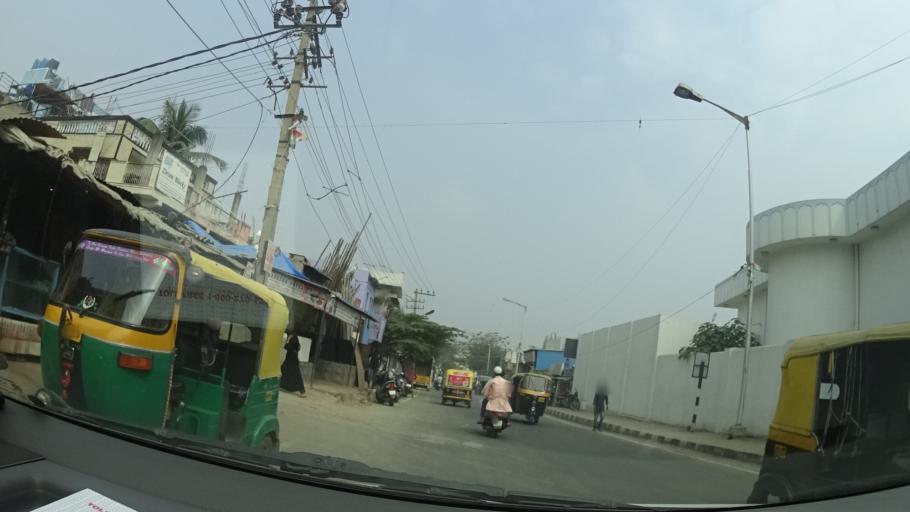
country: IN
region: Karnataka
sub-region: Bangalore Urban
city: Bangalore
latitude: 13.0234
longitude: 77.6195
